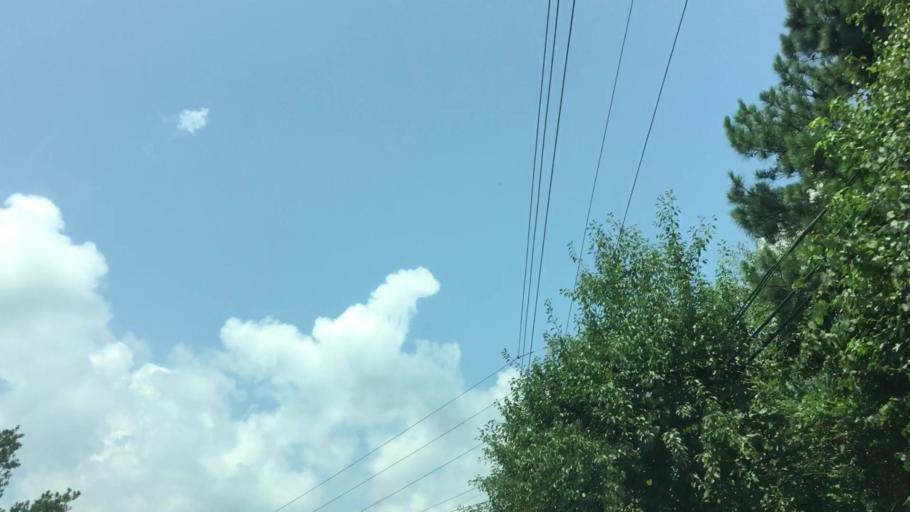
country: US
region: Georgia
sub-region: Fulton County
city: Chattahoochee Hills
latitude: 33.6150
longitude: -84.8400
